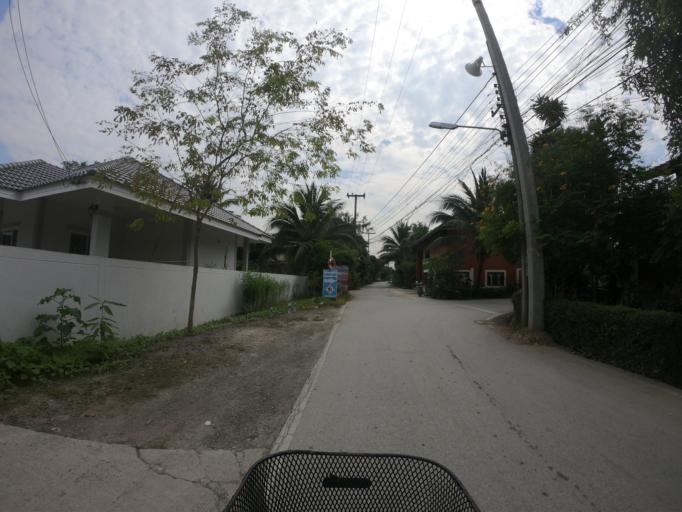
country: TH
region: Chiang Mai
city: Saraphi
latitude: 18.7035
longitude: 99.0389
